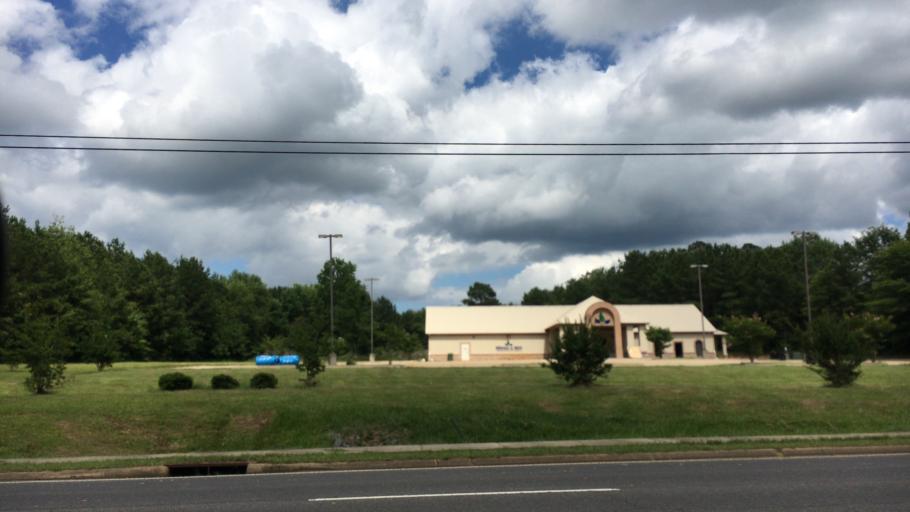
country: US
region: Louisiana
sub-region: Lincoln Parish
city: Ruston
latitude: 32.5008
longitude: -92.6369
